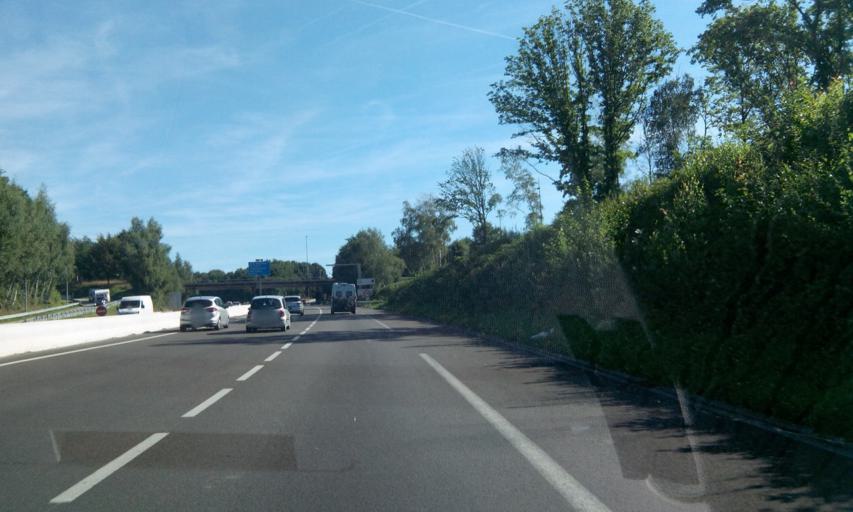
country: FR
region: Limousin
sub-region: Departement de la Haute-Vienne
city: Le Palais-sur-Vienne
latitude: 45.8587
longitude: 1.2845
